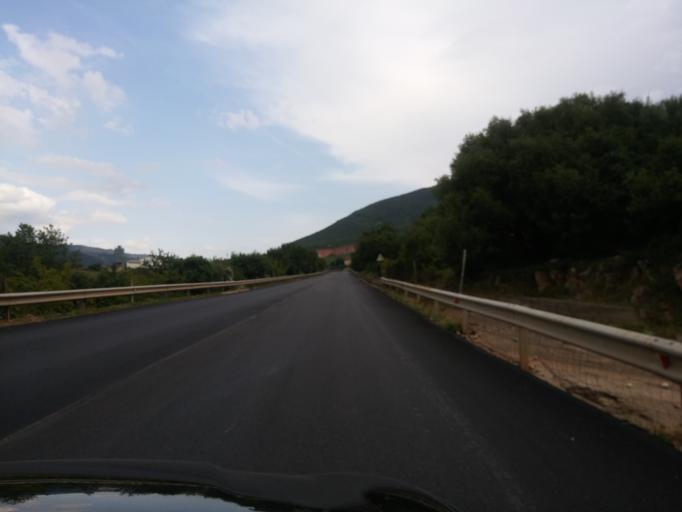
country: IT
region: Apulia
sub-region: Provincia di Foggia
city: Rignano Garganico
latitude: 41.7143
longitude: 15.5499
